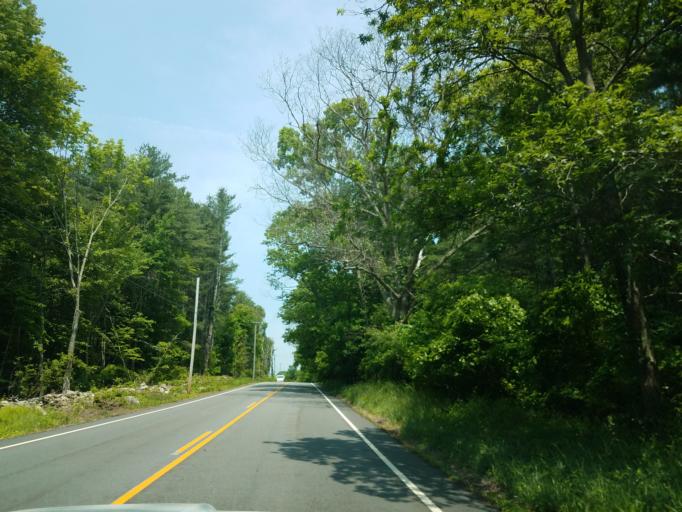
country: US
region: Connecticut
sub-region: Windham County
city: Plainfield
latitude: 41.6169
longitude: -71.8425
